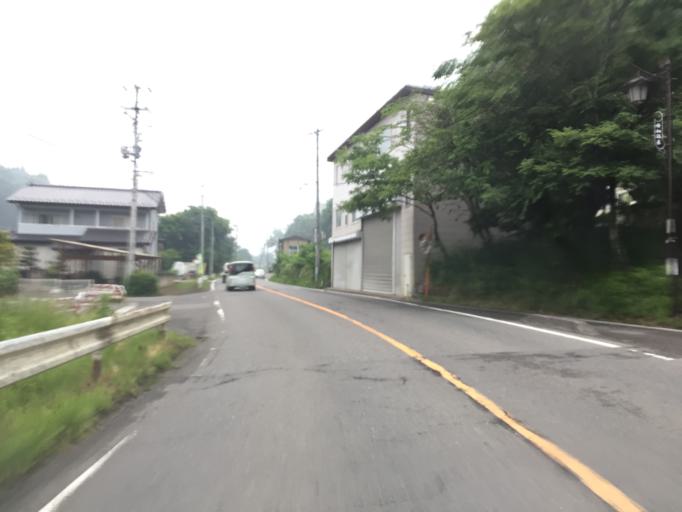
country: JP
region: Fukushima
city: Ishikawa
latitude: 37.1618
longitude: 140.4688
